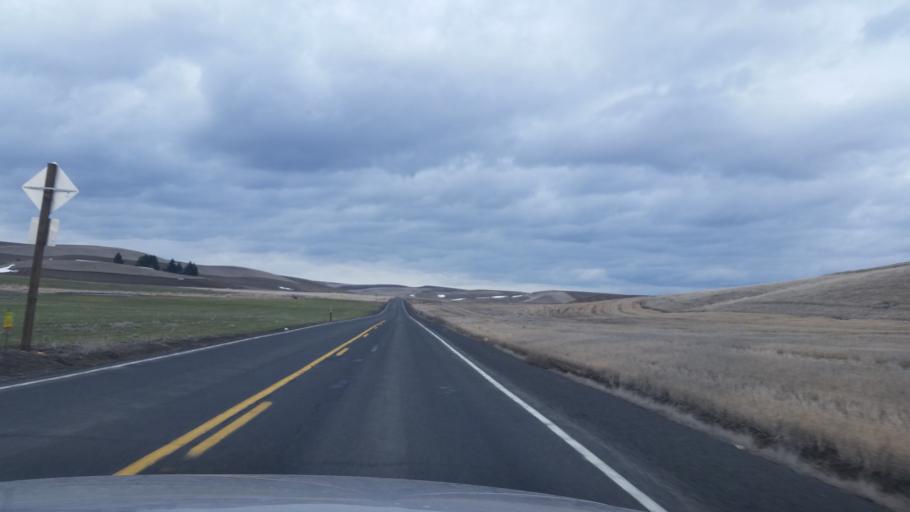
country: US
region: Washington
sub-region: Spokane County
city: Cheney
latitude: 47.1597
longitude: -117.8711
